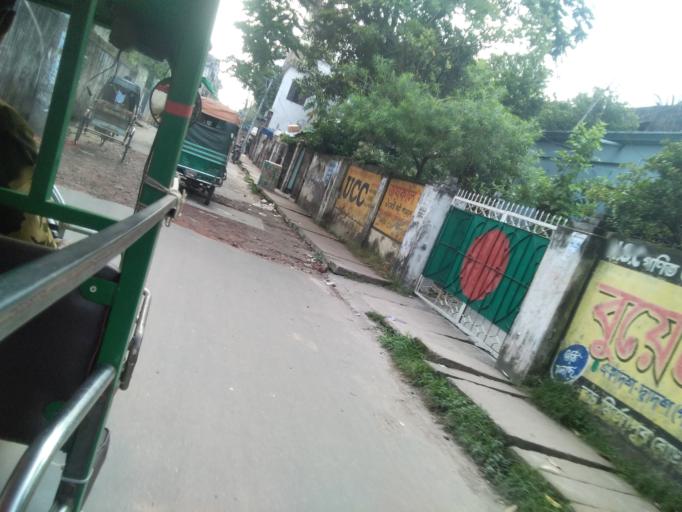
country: BD
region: Khulna
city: Khulna
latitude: 22.8132
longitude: 89.5607
